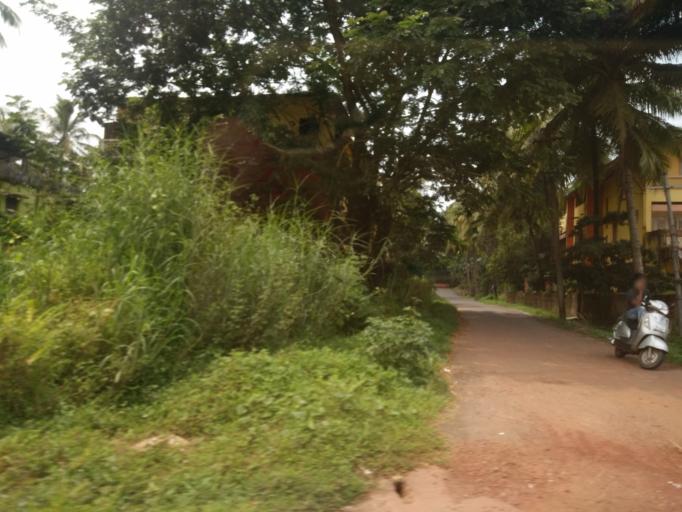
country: IN
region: Goa
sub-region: South Goa
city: Madgaon
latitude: 15.2482
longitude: 73.9707
